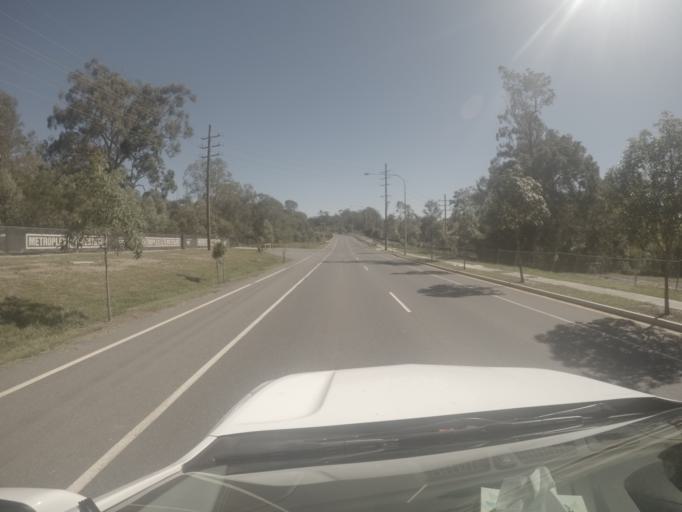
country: AU
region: Queensland
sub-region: Brisbane
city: Wacol
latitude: -27.5860
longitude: 152.9389
